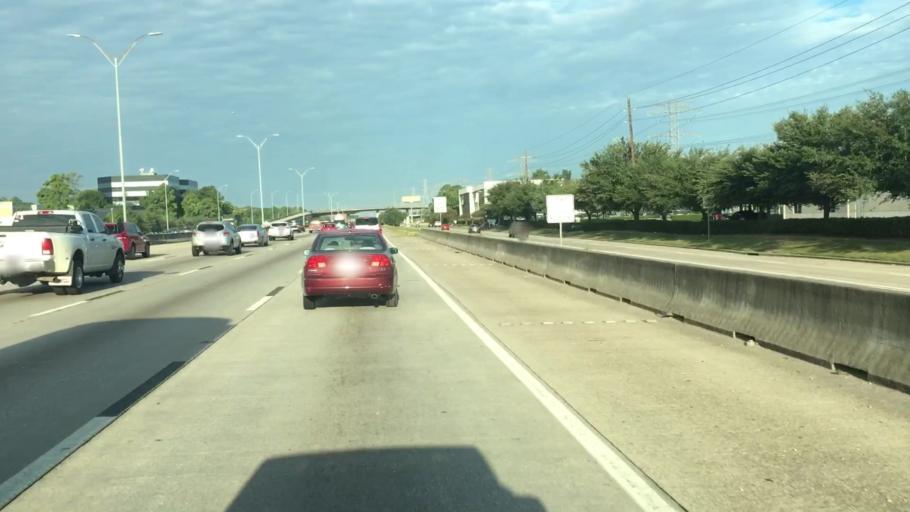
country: US
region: Texas
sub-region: Harris County
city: Aldine
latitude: 29.9382
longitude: -95.3220
